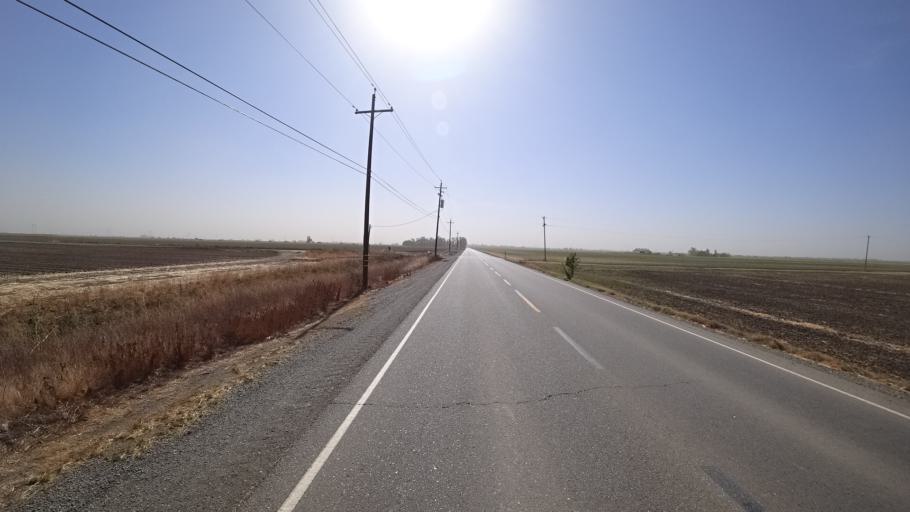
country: US
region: California
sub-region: Yolo County
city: Davis
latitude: 38.5830
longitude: -121.6750
